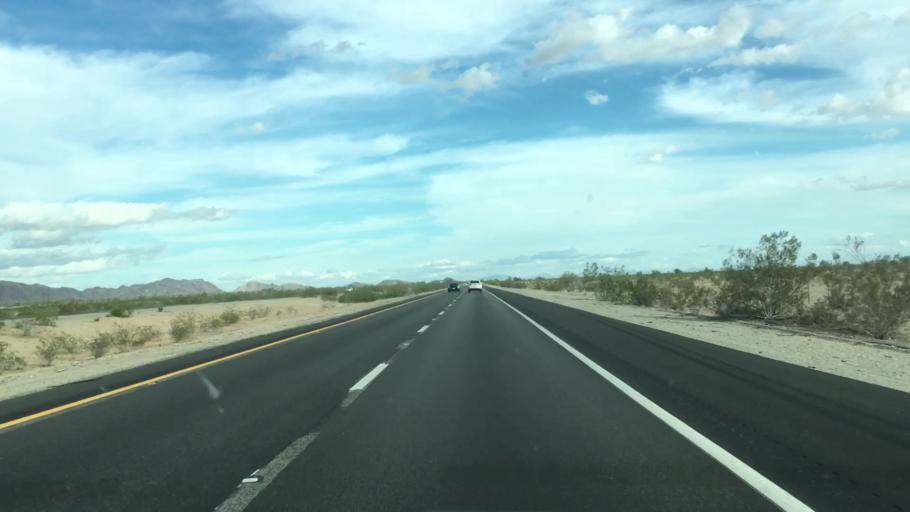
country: US
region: California
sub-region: Riverside County
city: Mesa Verde
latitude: 33.6091
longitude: -114.8574
